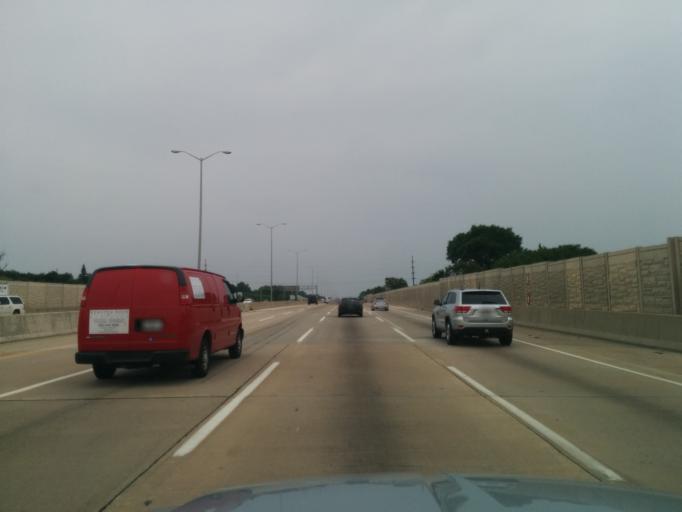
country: US
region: Illinois
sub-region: DuPage County
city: Lisle
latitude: 41.8057
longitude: -88.0907
